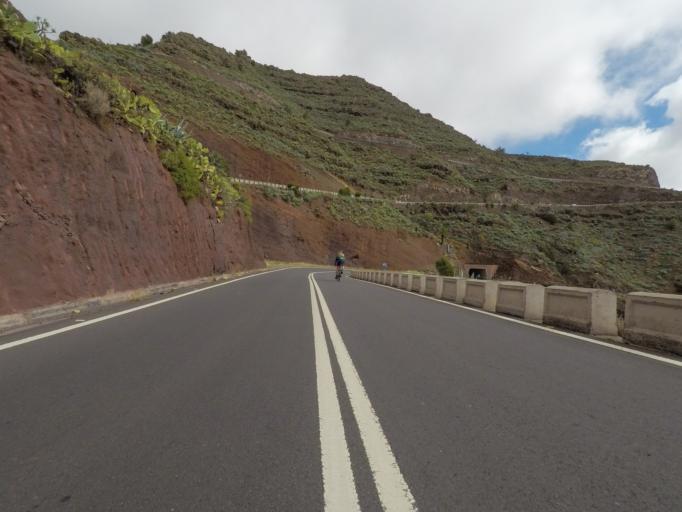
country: ES
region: Canary Islands
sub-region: Provincia de Santa Cruz de Tenerife
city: Vallehermosa
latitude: 28.1177
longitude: -17.3224
